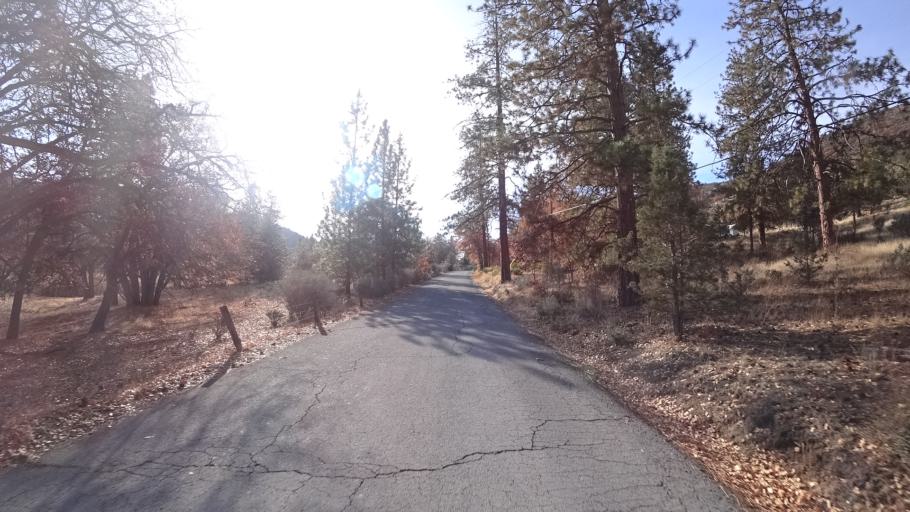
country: US
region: California
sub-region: Siskiyou County
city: Montague
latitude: 41.6152
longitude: -122.5779
